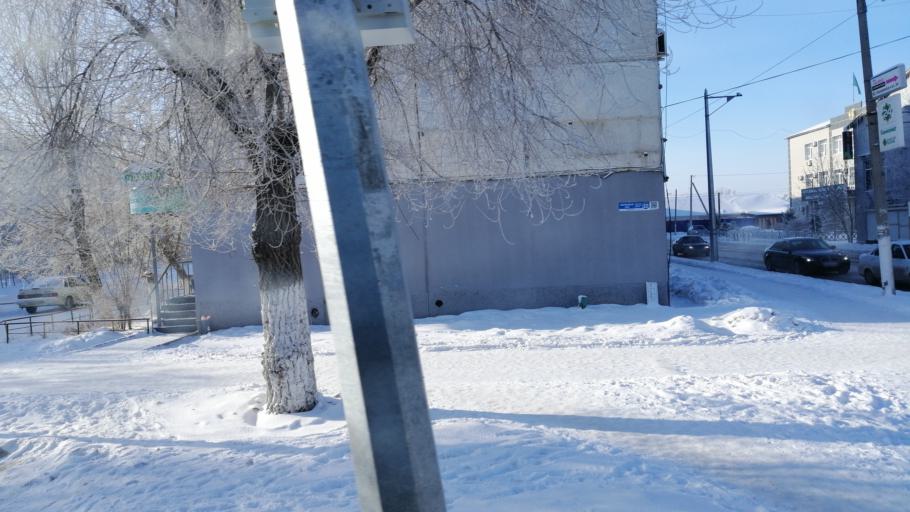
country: KZ
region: Aqtoebe
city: Aqtobe
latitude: 50.3055
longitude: 57.1506
